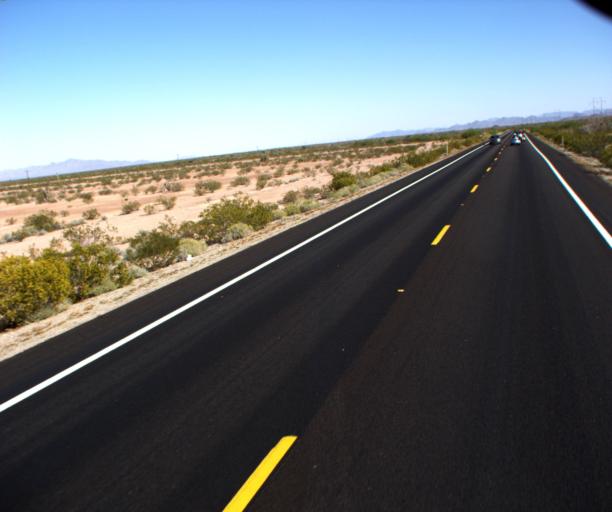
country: US
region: Arizona
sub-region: La Paz County
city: Quartzsite
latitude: 33.2980
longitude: -114.2214
